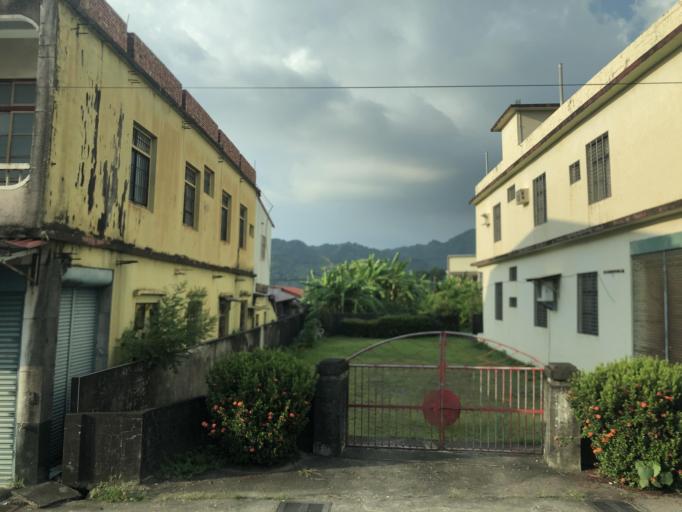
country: TW
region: Taiwan
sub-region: Pingtung
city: Pingtung
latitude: 22.8867
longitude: 120.5280
